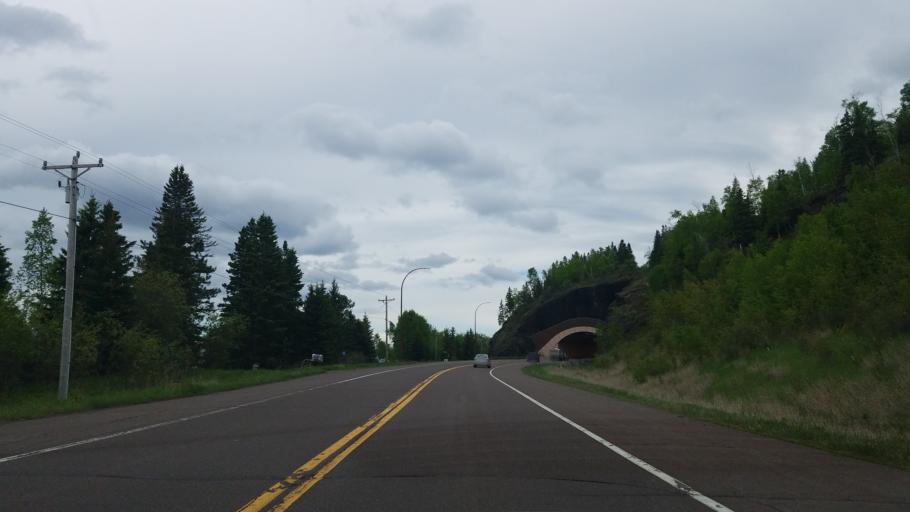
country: US
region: Minnesota
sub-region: Lake County
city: Two Harbors
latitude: 47.0980
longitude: -91.5489
